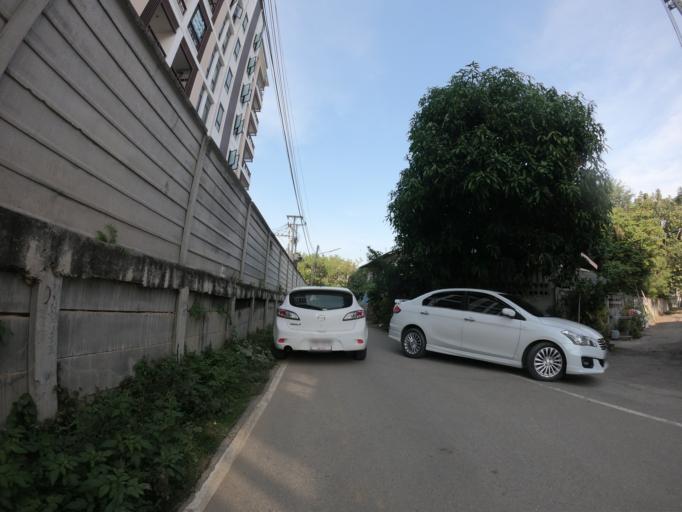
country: TH
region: Chiang Mai
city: San Sai
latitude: 18.8216
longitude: 99.0145
